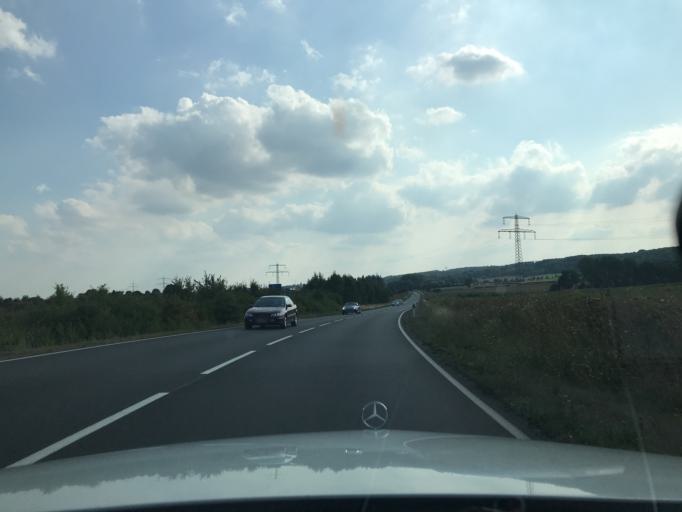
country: DE
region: Lower Saxony
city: Bovenden
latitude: 51.5677
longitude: 9.8830
